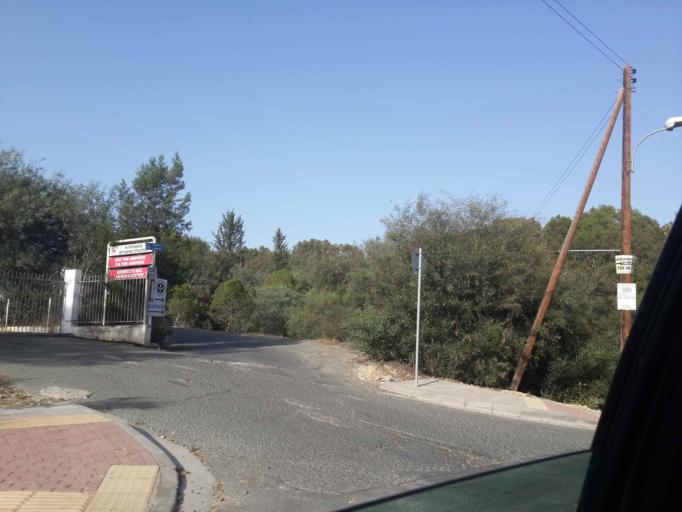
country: CY
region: Lefkosia
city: Nicosia
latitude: 35.1596
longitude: 33.3474
